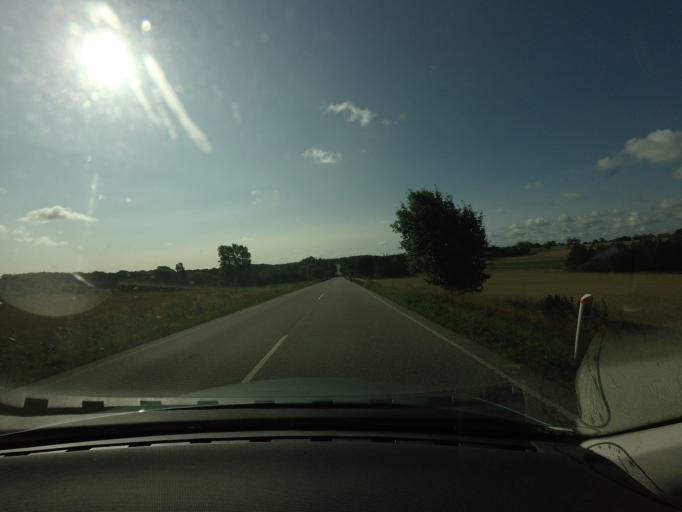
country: DK
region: Zealand
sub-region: Vordingborg Kommune
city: Praesto
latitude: 55.1030
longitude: 12.0717
